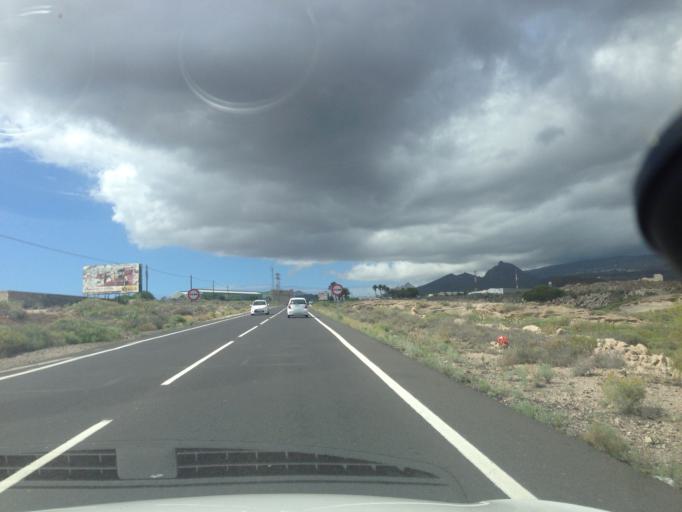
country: ES
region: Canary Islands
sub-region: Provincia de Santa Cruz de Tenerife
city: San Miguel
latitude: 28.0449
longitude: -16.6082
